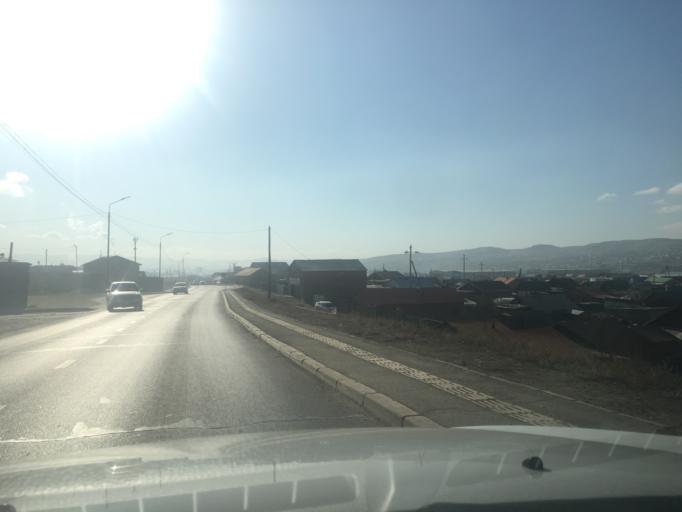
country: MN
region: Ulaanbaatar
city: Ulaanbaatar
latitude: 47.9618
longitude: 106.8278
